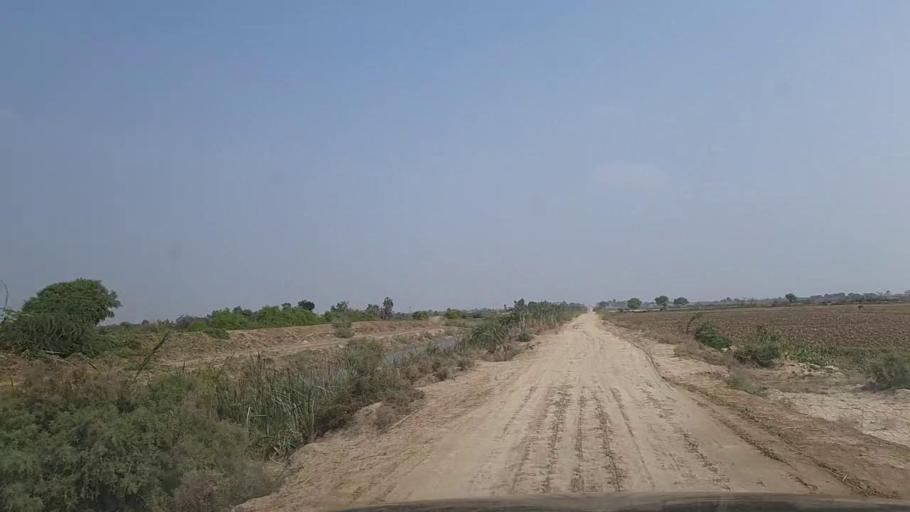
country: PK
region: Sindh
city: Thatta
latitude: 24.7606
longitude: 67.8107
